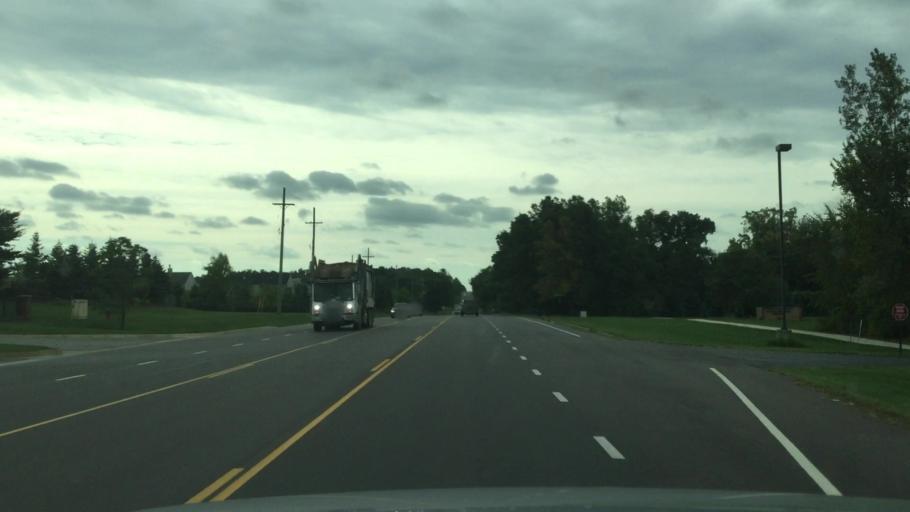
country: US
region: Michigan
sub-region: Livingston County
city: Howell
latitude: 42.6243
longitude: -83.8753
